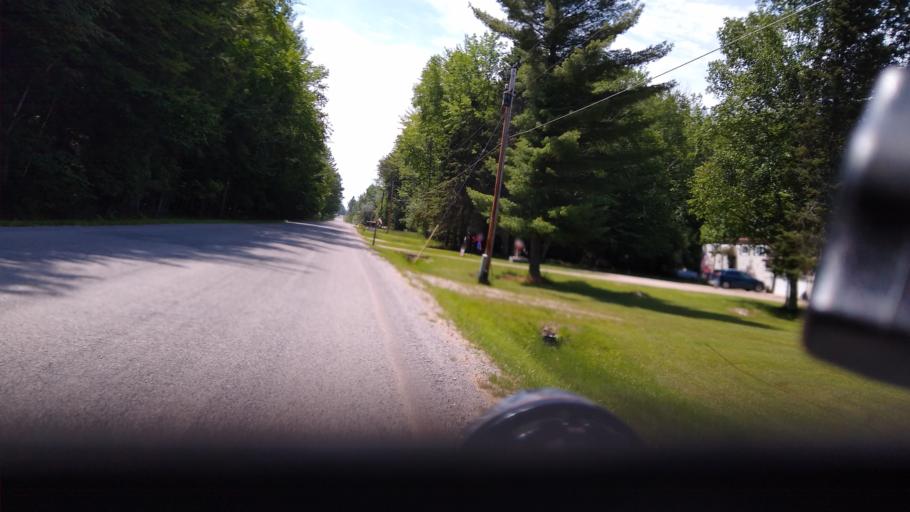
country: US
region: Michigan
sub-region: Delta County
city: Escanaba
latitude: 45.7101
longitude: -87.1396
